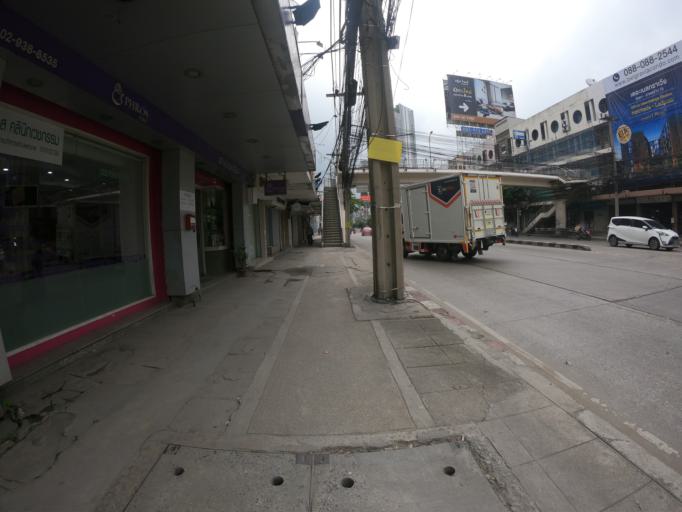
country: TH
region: Bangkok
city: Chatuchak
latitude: 13.8079
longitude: 100.5705
